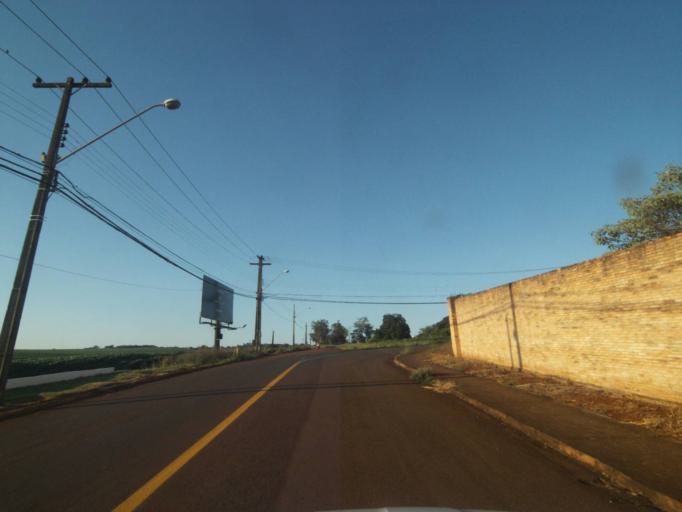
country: BR
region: Parana
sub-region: Londrina
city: Londrina
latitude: -23.3464
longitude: -51.1953
